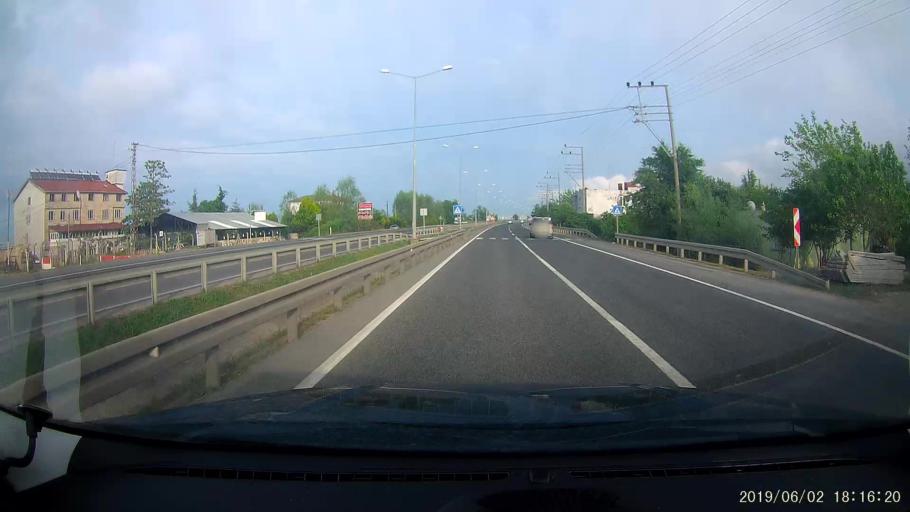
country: TR
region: Ordu
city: Unieh
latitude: 41.1015
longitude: 37.3964
